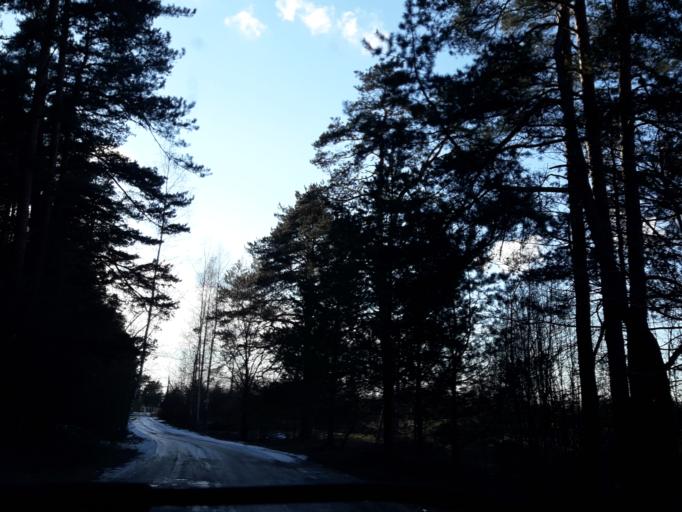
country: LV
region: Kekava
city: Kekava
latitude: 56.8737
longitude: 24.2117
